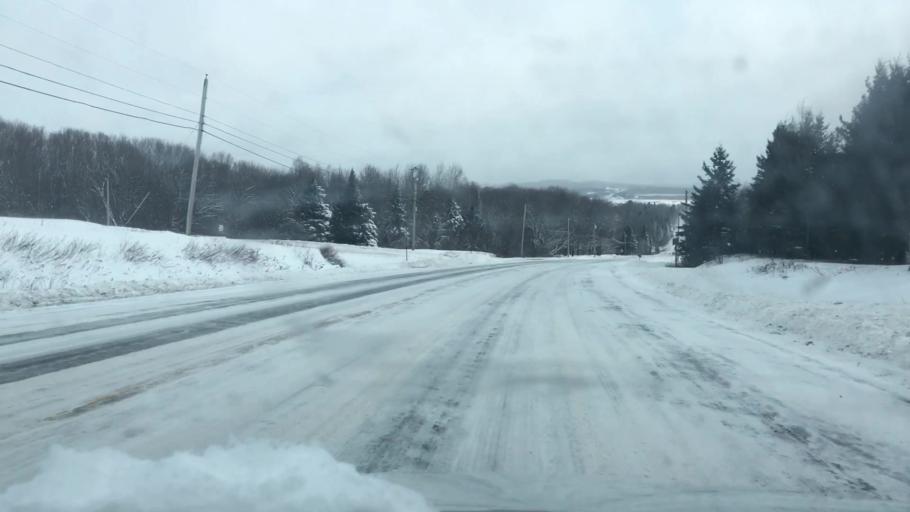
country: US
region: Maine
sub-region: Aroostook County
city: Van Buren
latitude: 47.1395
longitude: -67.9507
